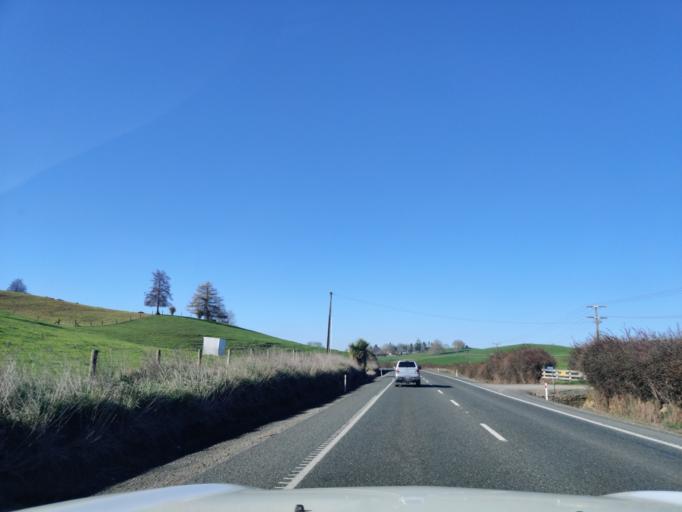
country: NZ
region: Waikato
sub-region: Matamata-Piako District
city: Matamata
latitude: -38.0047
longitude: 175.7689
